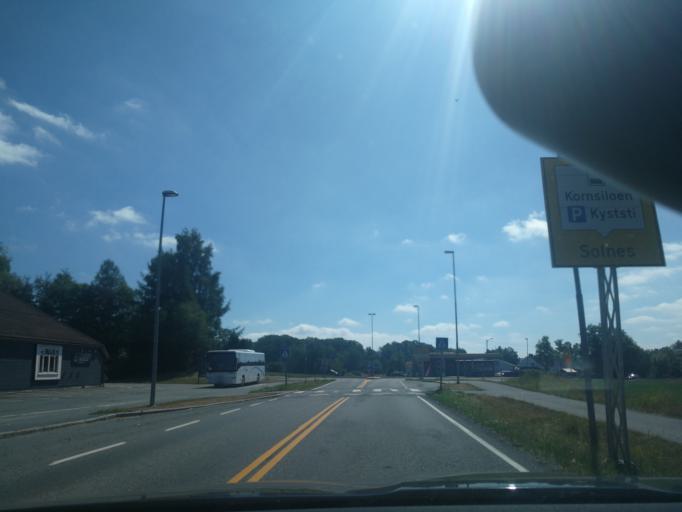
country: NO
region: Vestfold
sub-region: Stokke
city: Melsomvik
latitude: 59.2254
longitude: 10.3350
